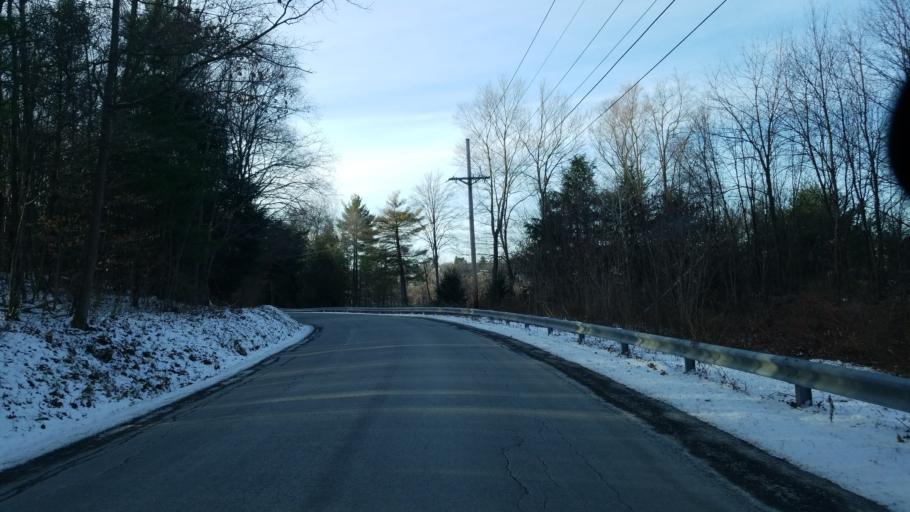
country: US
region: Pennsylvania
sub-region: Clearfield County
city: DuBois
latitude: 41.1208
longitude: -78.7114
